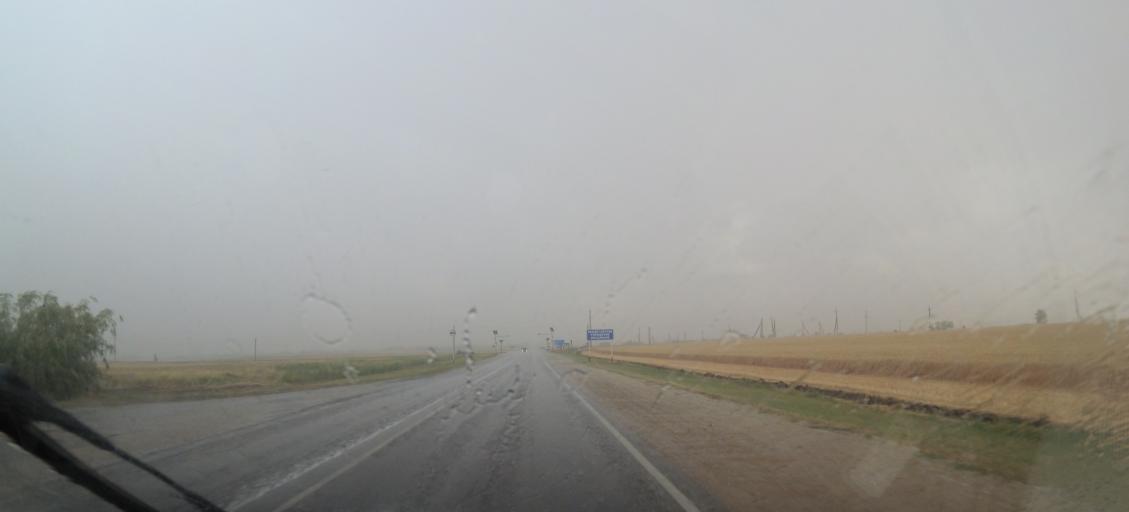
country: RU
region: Rostov
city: Proletarsk
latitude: 46.6764
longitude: 41.7020
